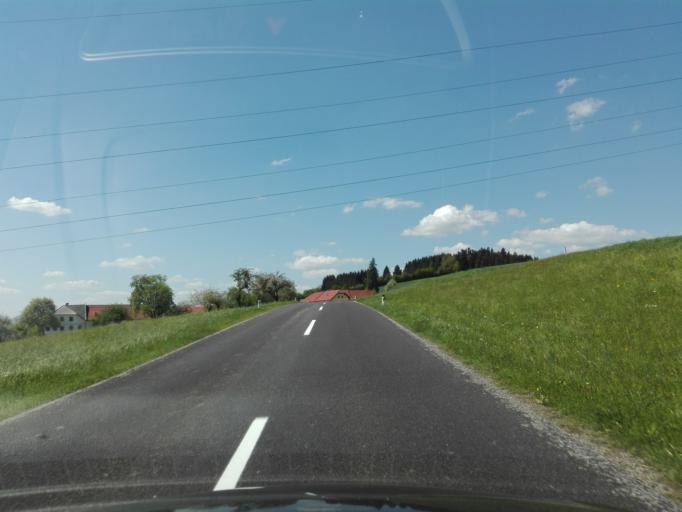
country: AT
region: Upper Austria
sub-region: Politischer Bezirk Rohrbach
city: Kleinzell im Muehlkreis
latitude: 48.3616
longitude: 13.9347
